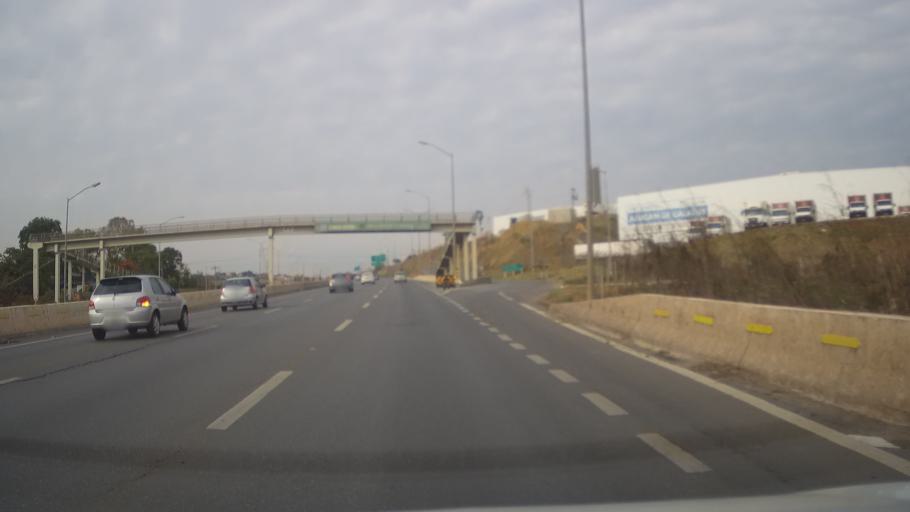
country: BR
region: Minas Gerais
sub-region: Vespasiano
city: Vespasiano
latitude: -19.7332
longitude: -43.9441
